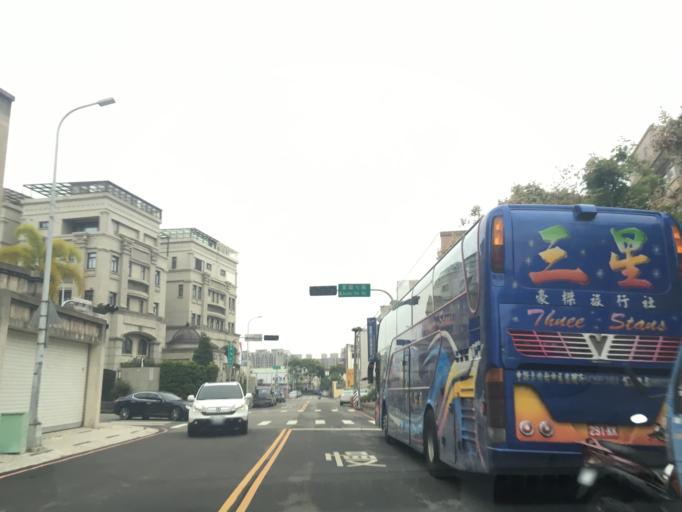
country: TW
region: Taiwan
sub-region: Taichung City
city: Taichung
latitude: 24.1663
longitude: 120.7136
